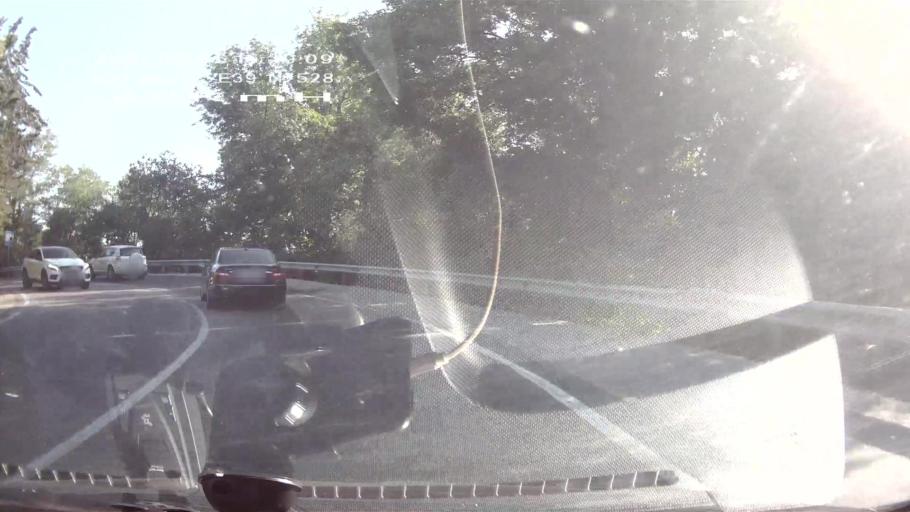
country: RU
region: Krasnodarskiy
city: Tuapse
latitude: 44.0918
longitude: 39.1175
